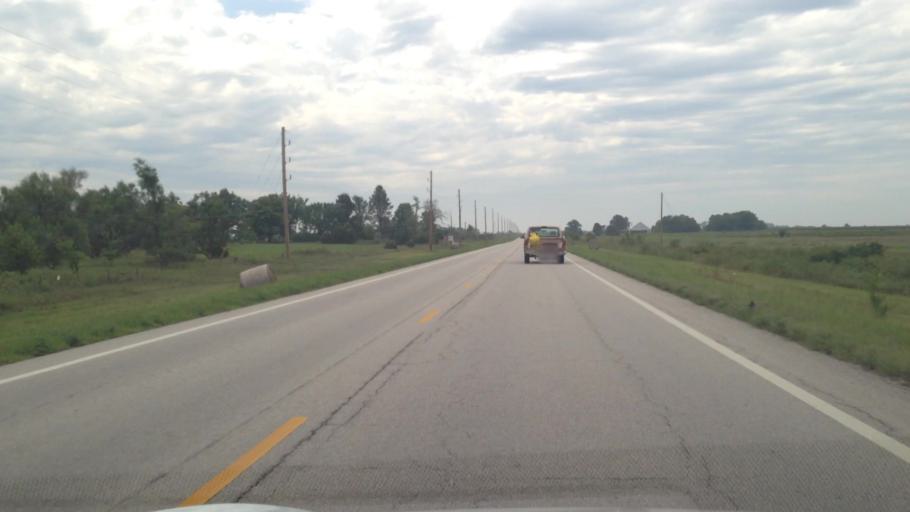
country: US
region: Kansas
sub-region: Allen County
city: Iola
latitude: 37.9479
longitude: -95.1700
